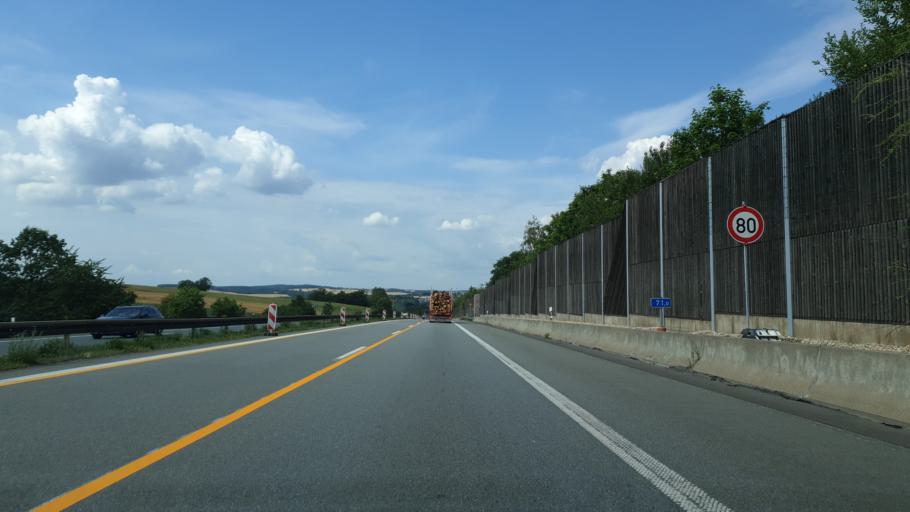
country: DE
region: Saxony
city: Wilkau-Hasslau
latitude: 50.6766
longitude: 12.5420
